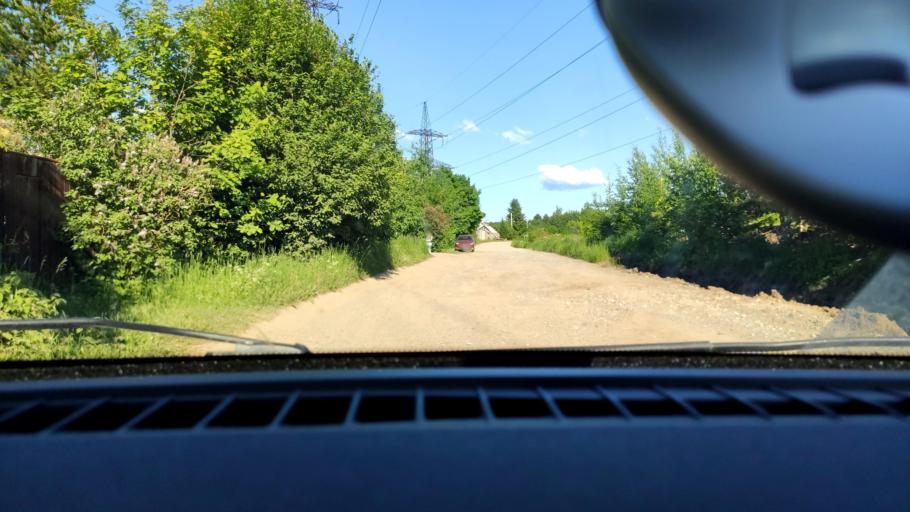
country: RU
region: Perm
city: Ferma
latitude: 57.9159
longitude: 56.3538
